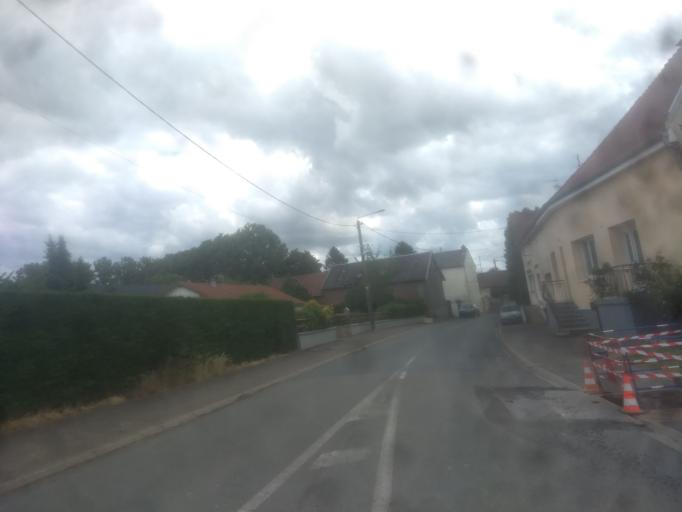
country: FR
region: Nord-Pas-de-Calais
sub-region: Departement du Pas-de-Calais
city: Agny
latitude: 50.2276
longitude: 2.7393
